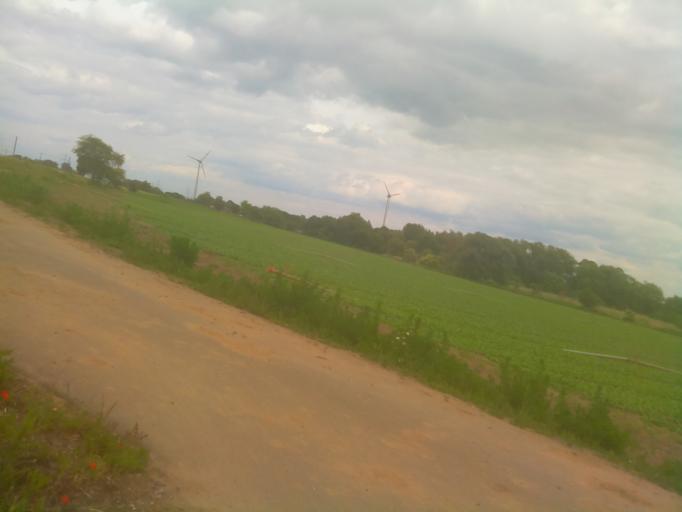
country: DE
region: Rheinland-Pfalz
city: Lambsheim
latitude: 49.5221
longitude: 8.2950
